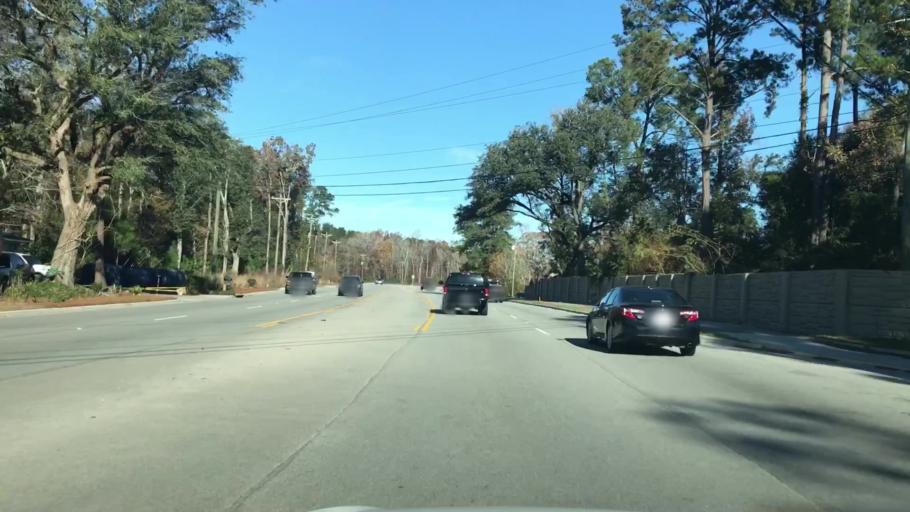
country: US
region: South Carolina
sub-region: Dorchester County
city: Centerville
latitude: 32.9618
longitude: -80.2010
